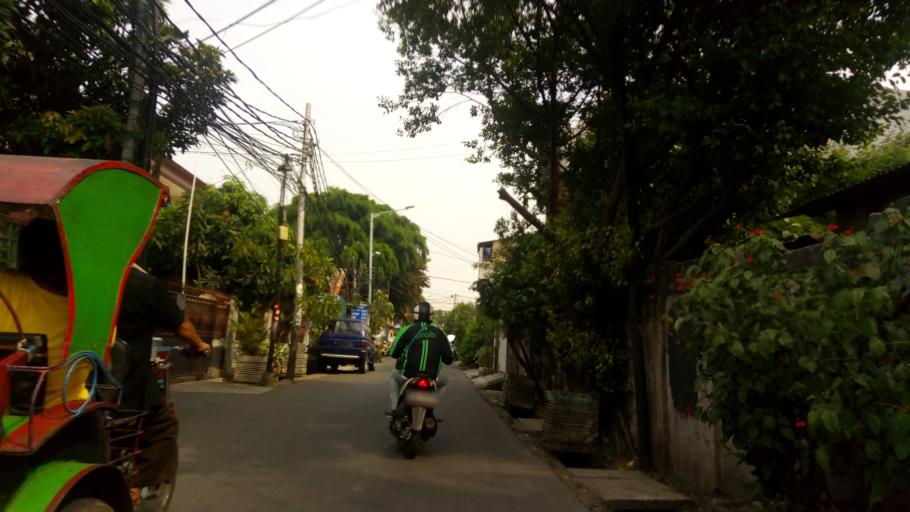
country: ID
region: Jakarta Raya
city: Jakarta
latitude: -6.1698
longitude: 106.8492
